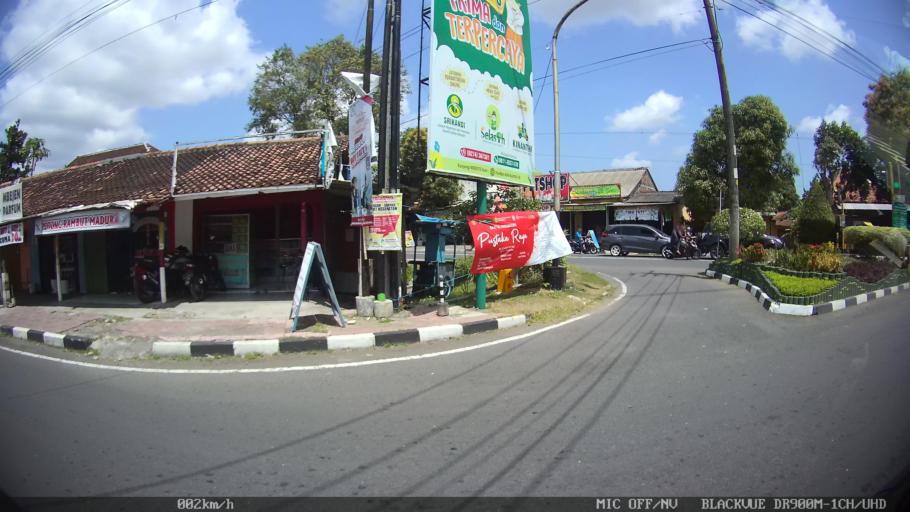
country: ID
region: Daerah Istimewa Yogyakarta
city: Bantul
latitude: -7.8931
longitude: 110.3349
